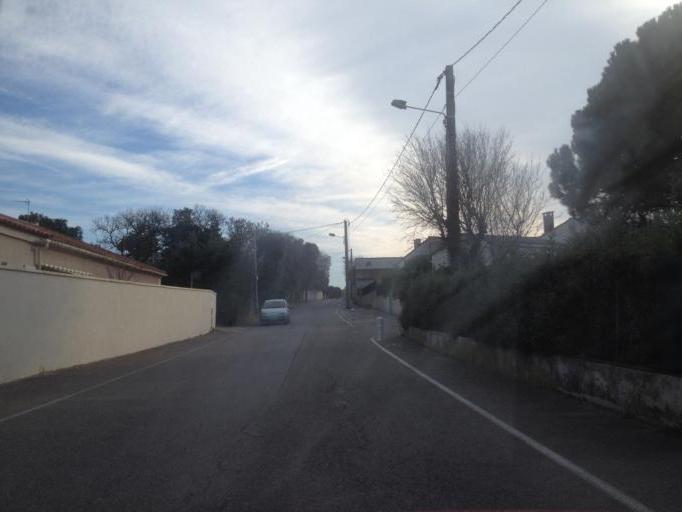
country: FR
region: Provence-Alpes-Cote d'Azur
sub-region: Departement du Vaucluse
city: Orange
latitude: 44.1221
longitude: 4.8267
